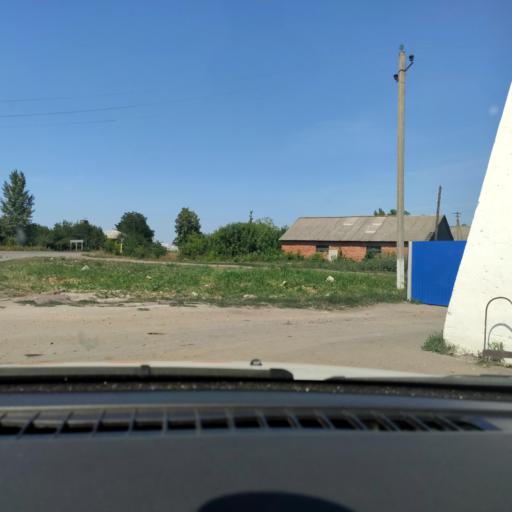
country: RU
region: Voronezj
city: Ostrogozhsk
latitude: 50.7061
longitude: 39.3334
